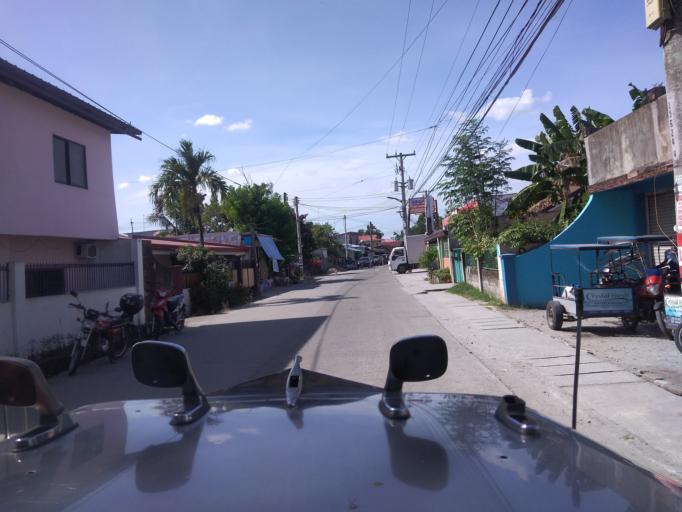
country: PH
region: Central Luzon
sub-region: Province of Pampanga
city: Magliman
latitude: 15.0361
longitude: 120.6629
